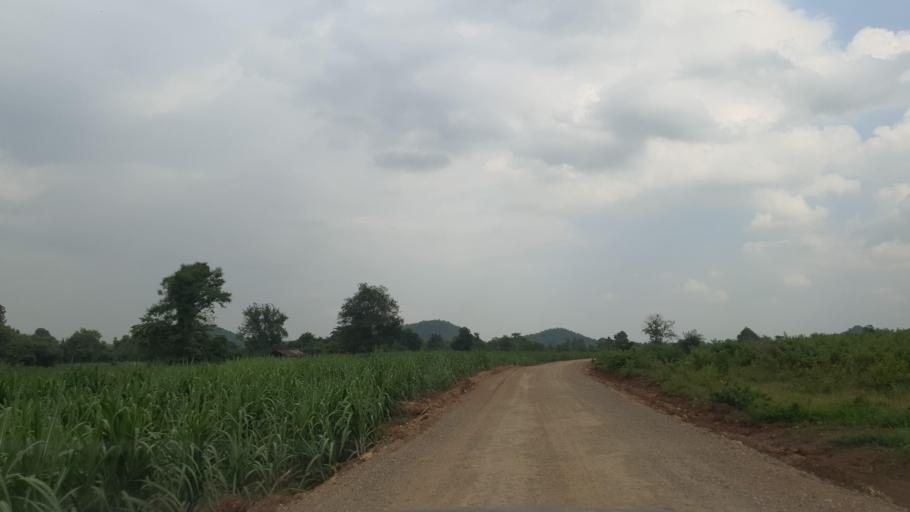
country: TH
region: Sukhothai
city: Thung Saliam
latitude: 17.2549
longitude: 99.5420
